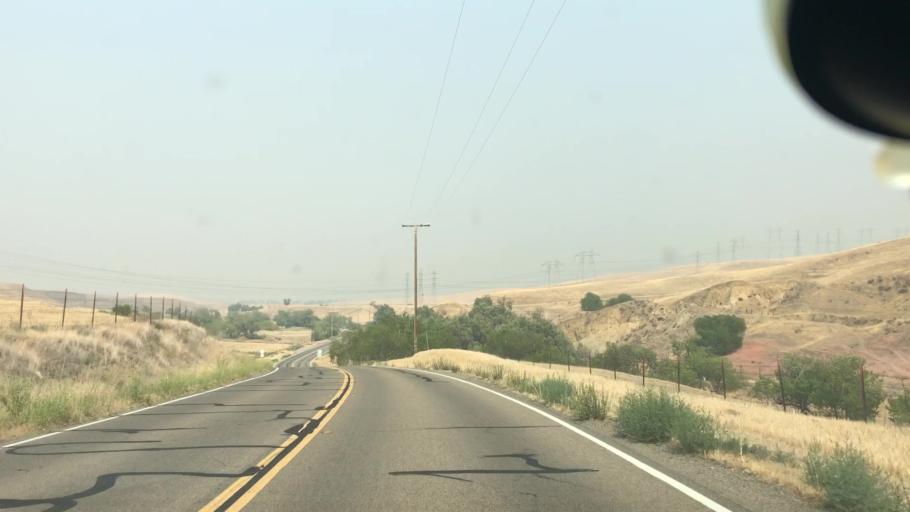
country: US
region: California
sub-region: San Joaquin County
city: Tracy
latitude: 37.6567
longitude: -121.4800
